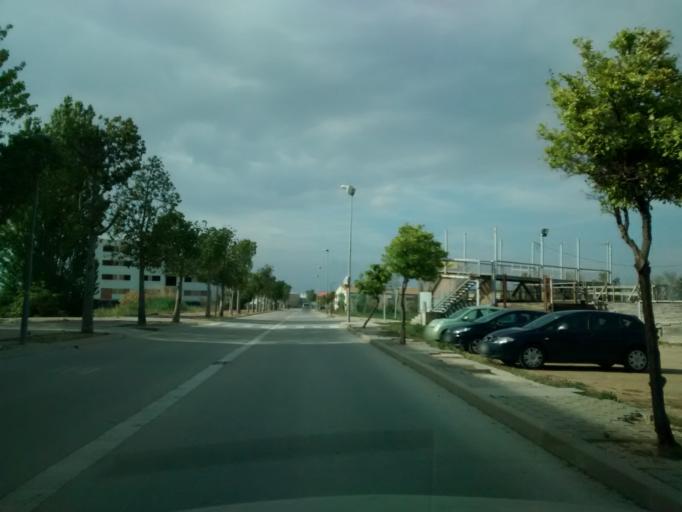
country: ES
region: Catalonia
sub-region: Provincia de Tarragona
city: Deltebre
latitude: 40.7218
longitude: 0.7211
